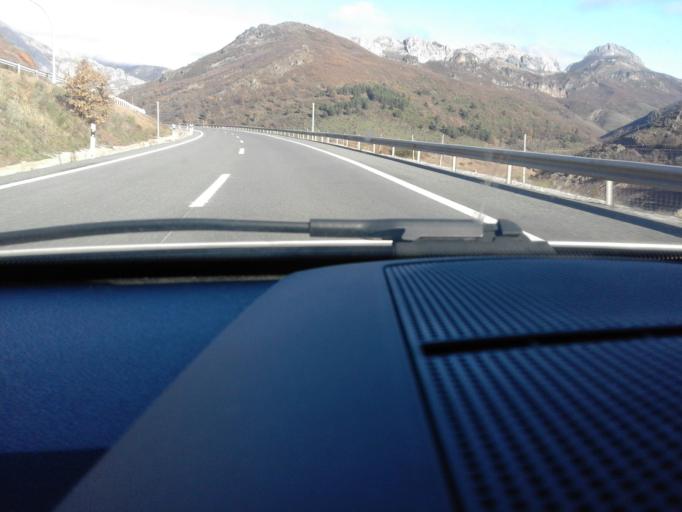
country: ES
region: Castille and Leon
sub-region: Provincia de Leon
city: Sena de Luna
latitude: 42.8896
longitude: -5.8874
